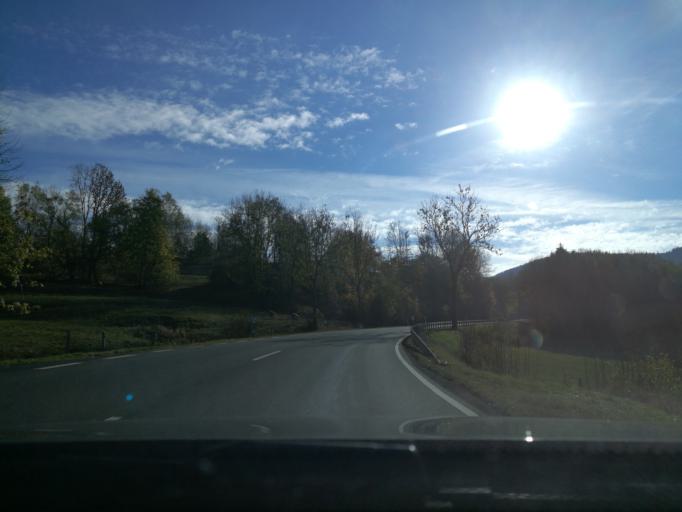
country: DE
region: Hesse
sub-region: Regierungsbezirk Kassel
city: Gersfeld
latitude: 50.4316
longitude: 9.9297
